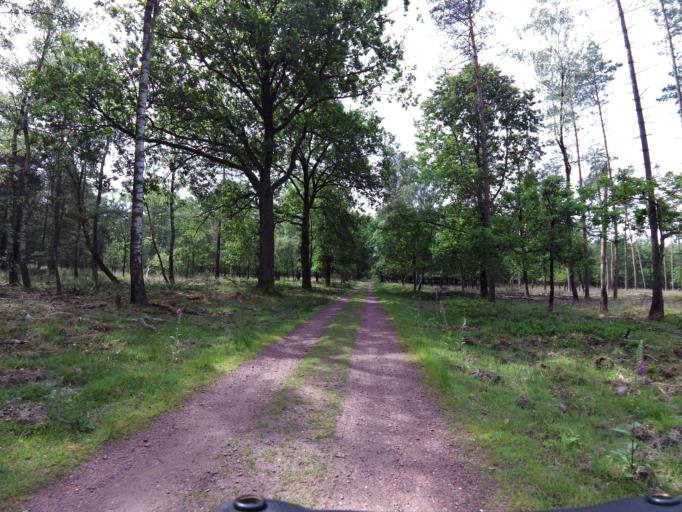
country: NL
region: Gelderland
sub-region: Gemeente Apeldoorn
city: Beekbergen
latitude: 52.0846
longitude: 5.9436
